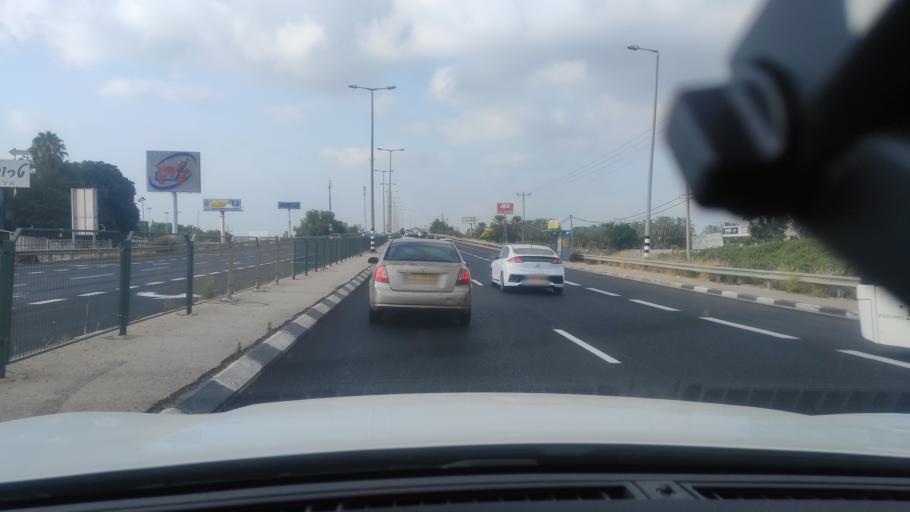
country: IL
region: Central District
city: Petah Tiqwa
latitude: 32.1156
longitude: 34.9029
